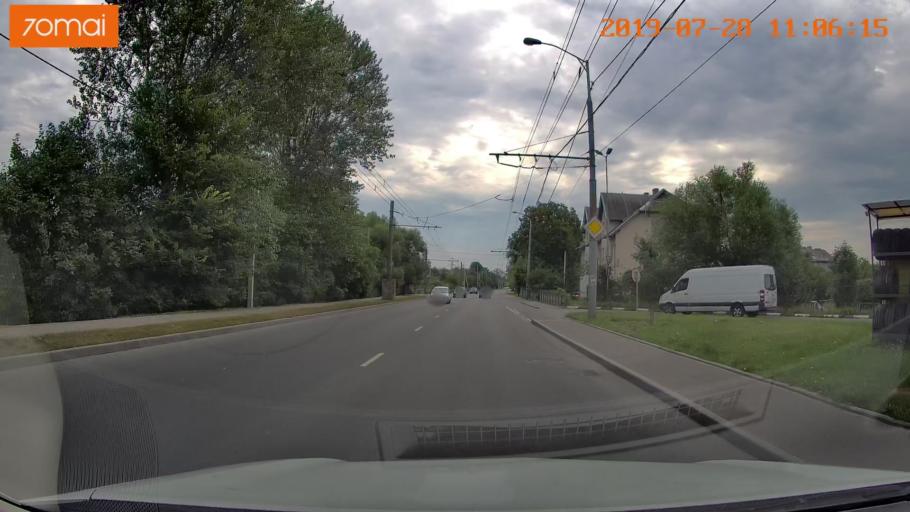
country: RU
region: Kaliningrad
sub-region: Gorod Kaliningrad
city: Kaliningrad
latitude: 54.7151
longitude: 20.4081
